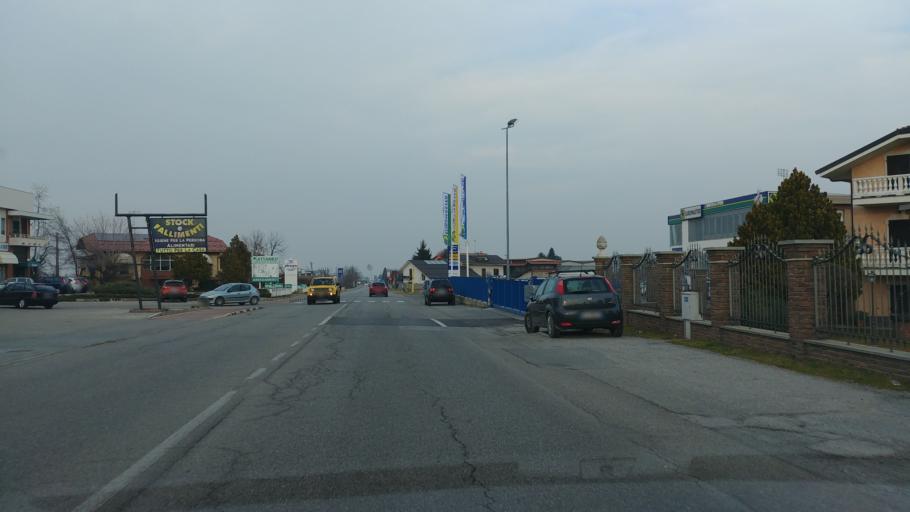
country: IT
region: Piedmont
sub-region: Provincia di Cuneo
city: Borgo San Dalmazzo
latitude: 44.3484
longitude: 7.5059
